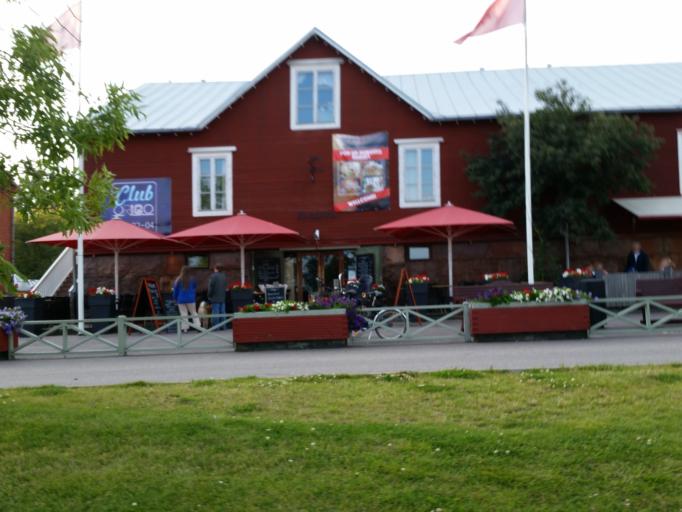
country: FI
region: Uusimaa
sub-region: Raaseporin
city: Hanko
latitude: 59.8212
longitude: 22.9627
